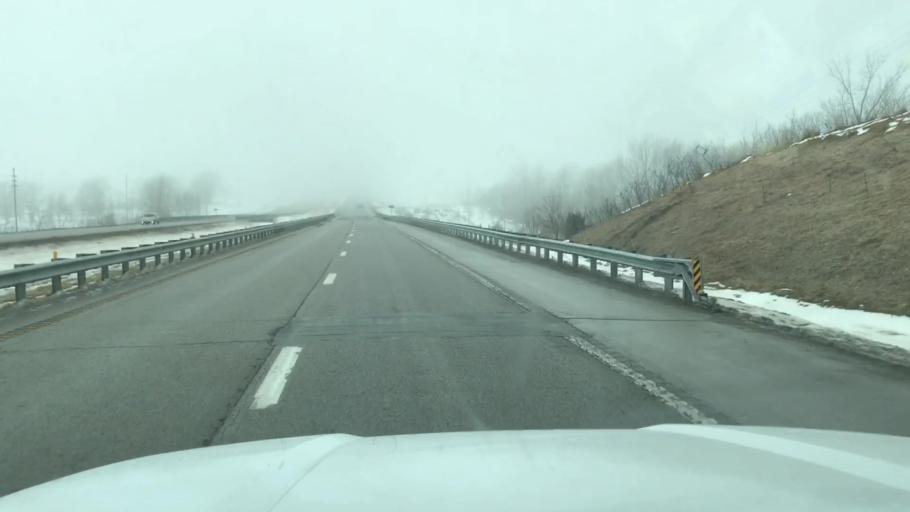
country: US
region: Missouri
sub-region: Clinton County
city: Cameron
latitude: 39.7550
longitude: -94.3144
